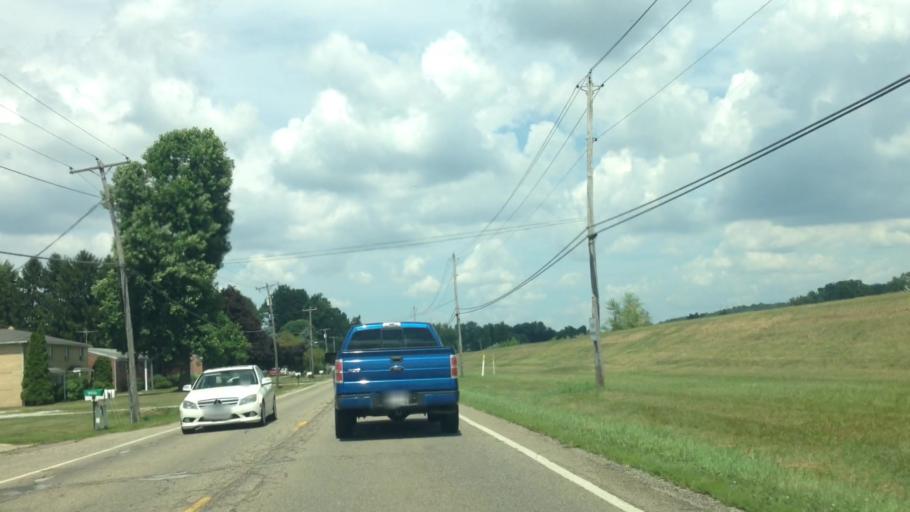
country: US
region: Ohio
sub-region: Summit County
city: New Franklin
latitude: 40.9502
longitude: -81.5339
